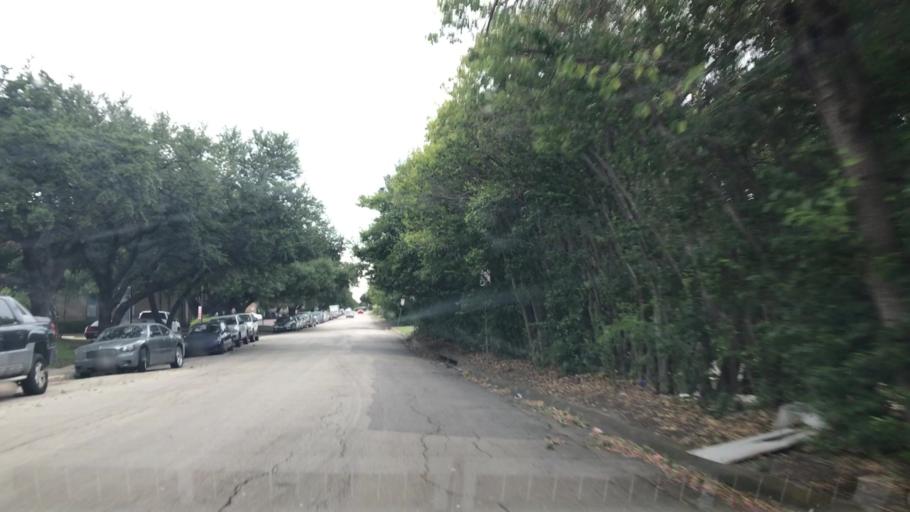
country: US
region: Texas
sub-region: Dallas County
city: Addison
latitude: 32.9596
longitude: -96.7901
